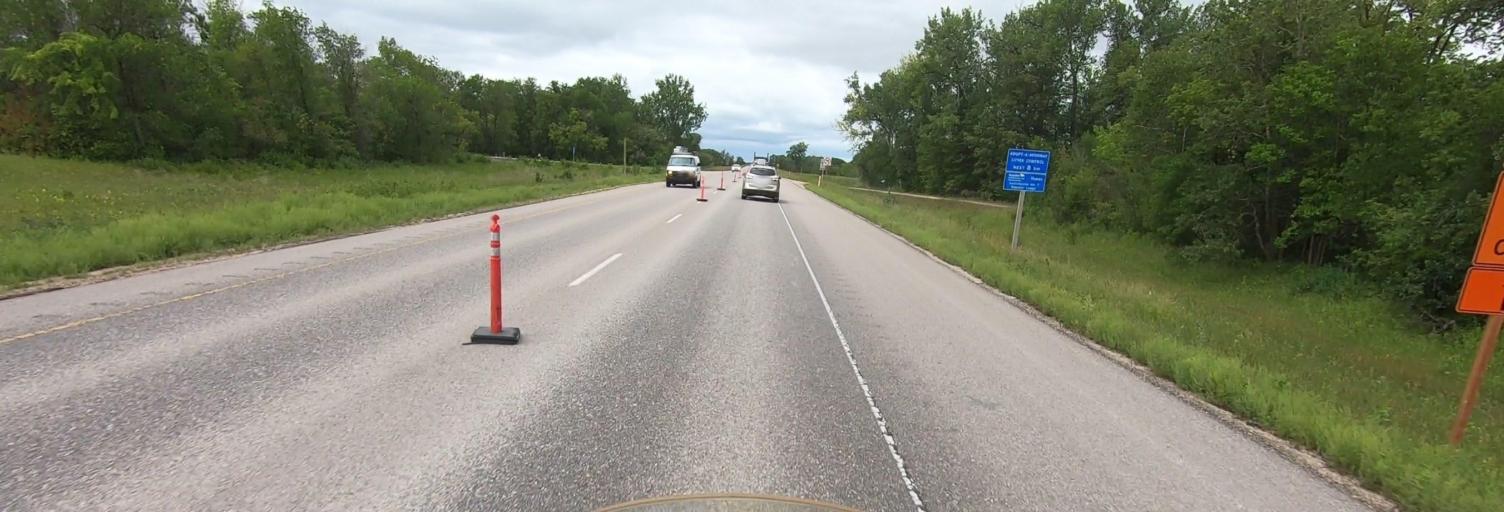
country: CA
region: Manitoba
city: Portage la Prairie
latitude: 49.9692
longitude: -98.0902
